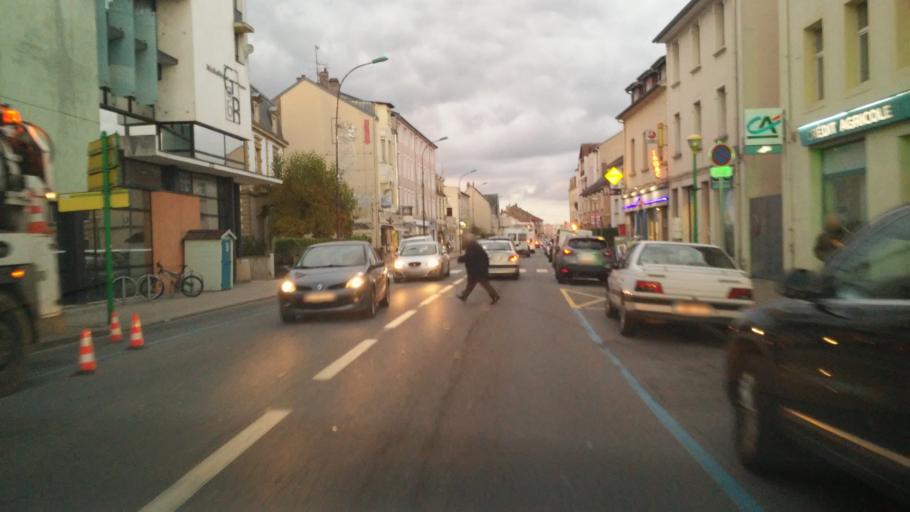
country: FR
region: Lorraine
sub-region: Departement de la Moselle
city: Maizieres-les-Metz
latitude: 49.2120
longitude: 6.1598
